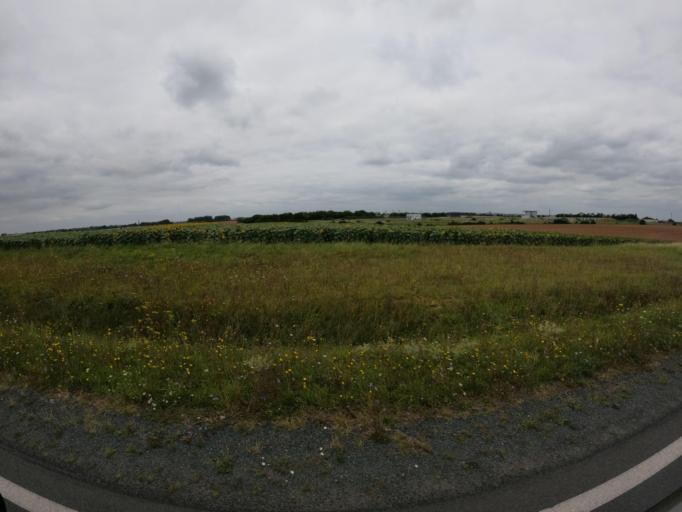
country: FR
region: Pays de la Loire
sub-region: Departement de la Vendee
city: Fontenay-le-Comte
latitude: 46.4440
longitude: -0.7811
